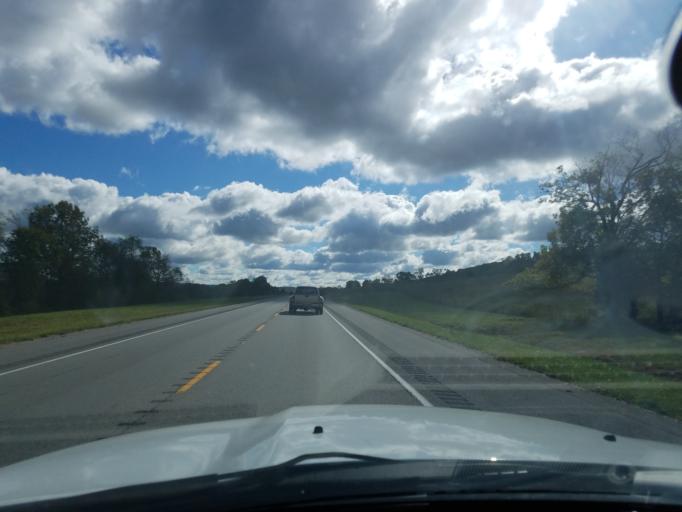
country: US
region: Kentucky
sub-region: Rockcastle County
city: Brodhead
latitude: 37.4490
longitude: -84.4899
